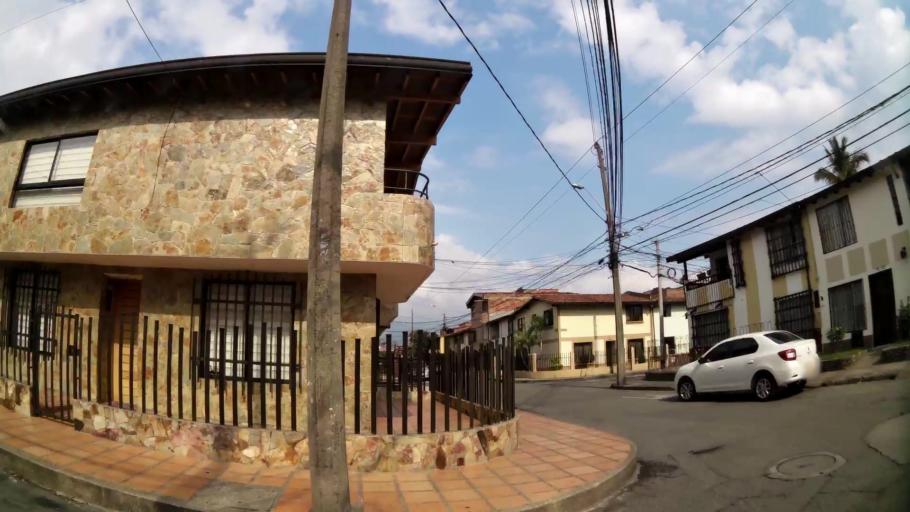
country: CO
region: Antioquia
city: Medellin
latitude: 6.2212
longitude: -75.5815
